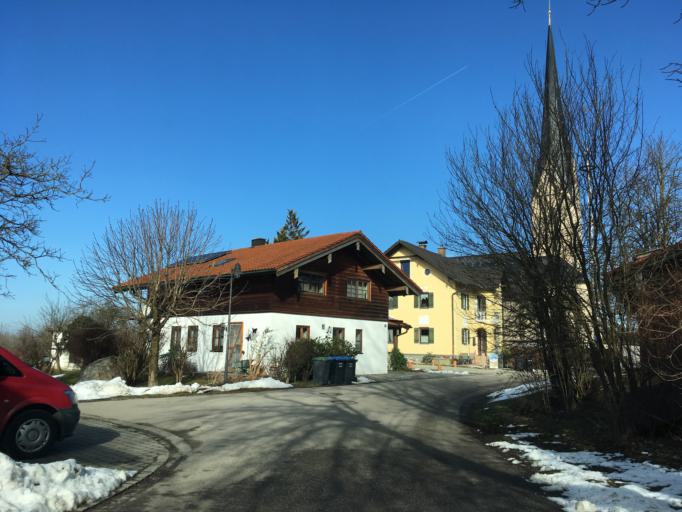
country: DE
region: Bavaria
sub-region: Upper Bavaria
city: Schechen
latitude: 47.9032
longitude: 12.1478
